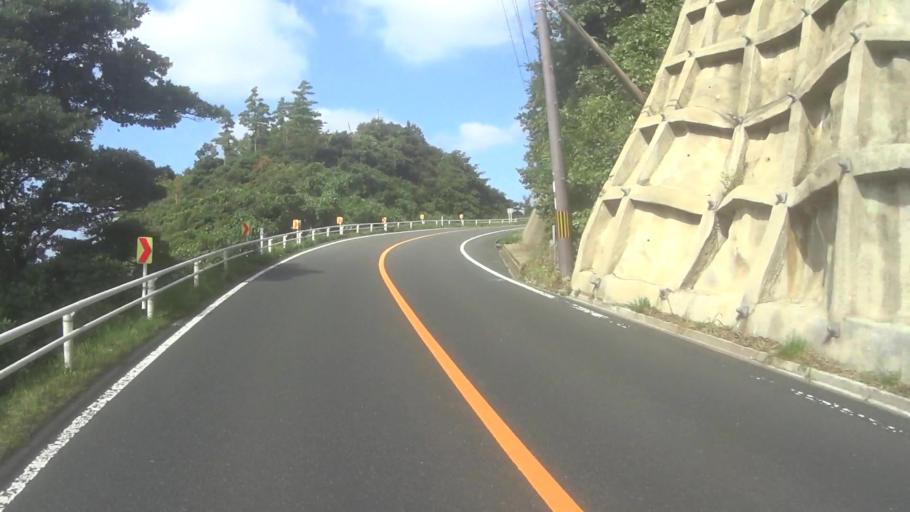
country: JP
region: Kyoto
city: Miyazu
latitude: 35.7469
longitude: 135.1302
